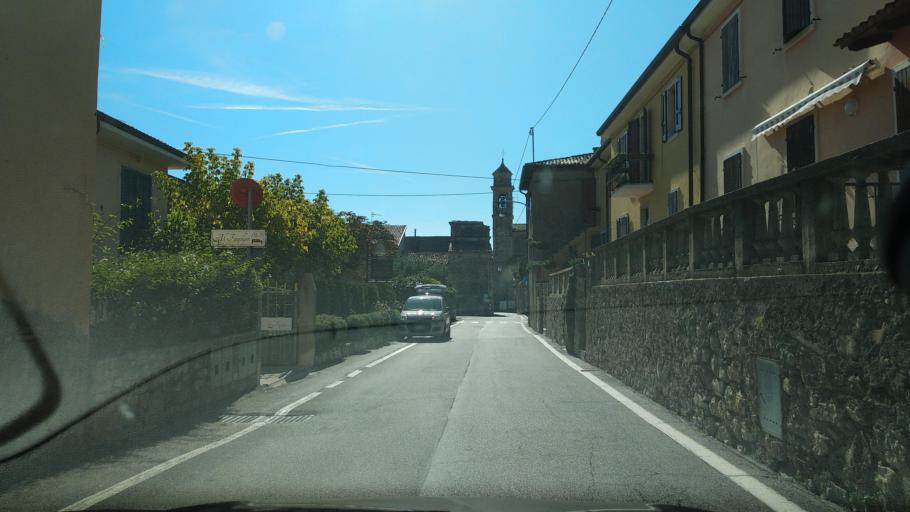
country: IT
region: Veneto
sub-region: Provincia di Verona
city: Torri del Benaco
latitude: 45.6130
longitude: 10.7025
